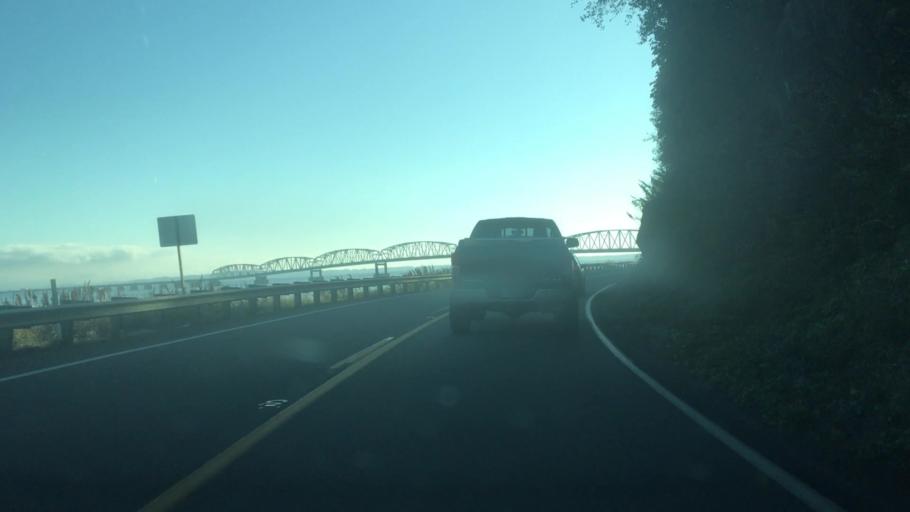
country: US
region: Oregon
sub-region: Clatsop County
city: Astoria
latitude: 46.2439
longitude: -123.8696
